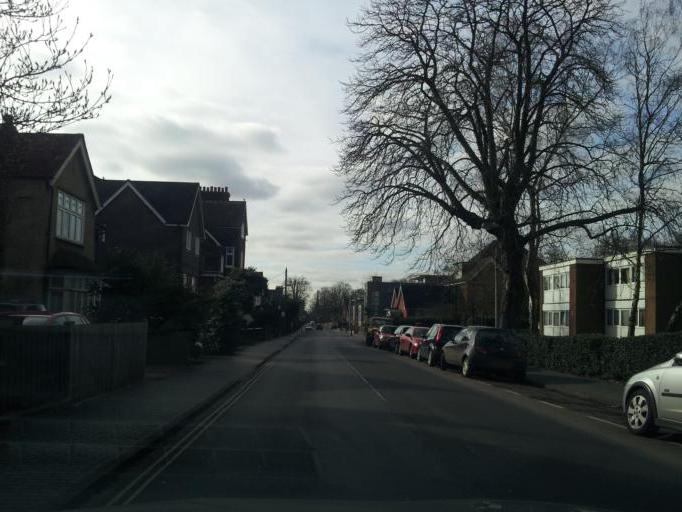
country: GB
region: England
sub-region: Hertfordshire
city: St Albans
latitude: 51.7551
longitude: -0.3269
